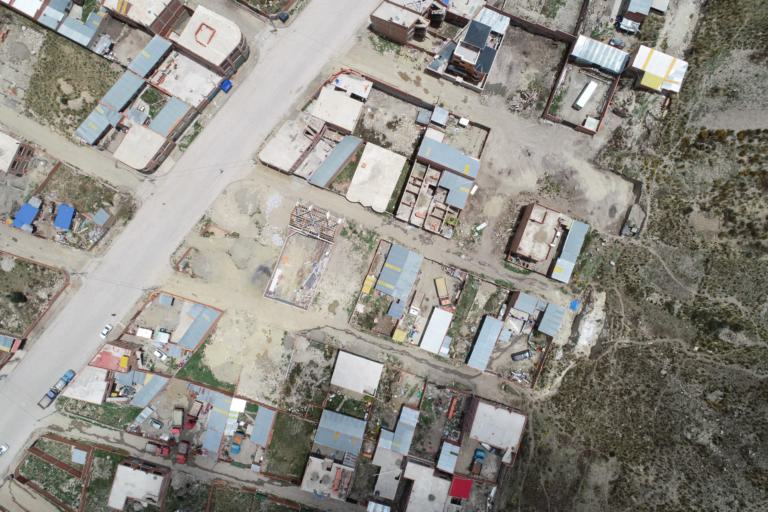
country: BO
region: La Paz
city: La Paz
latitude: -16.4404
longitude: -68.1429
